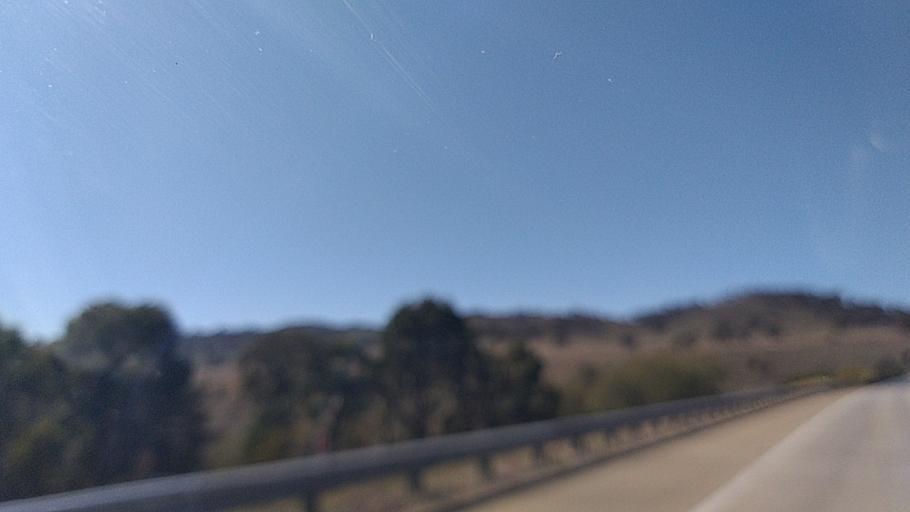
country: AU
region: New South Wales
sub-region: Yass Valley
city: Gundaroo
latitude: -35.1765
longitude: 149.2735
